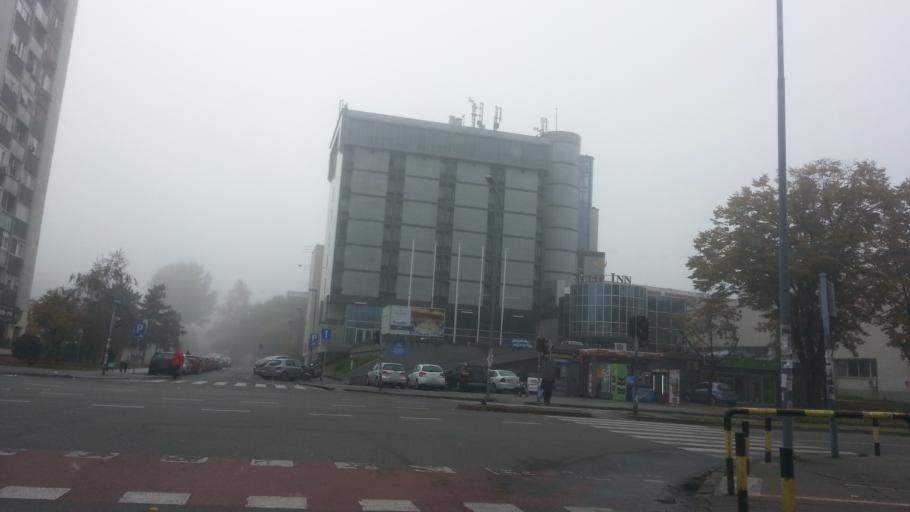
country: RS
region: Central Serbia
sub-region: Belgrade
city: Zemun
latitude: 44.8309
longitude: 20.4126
